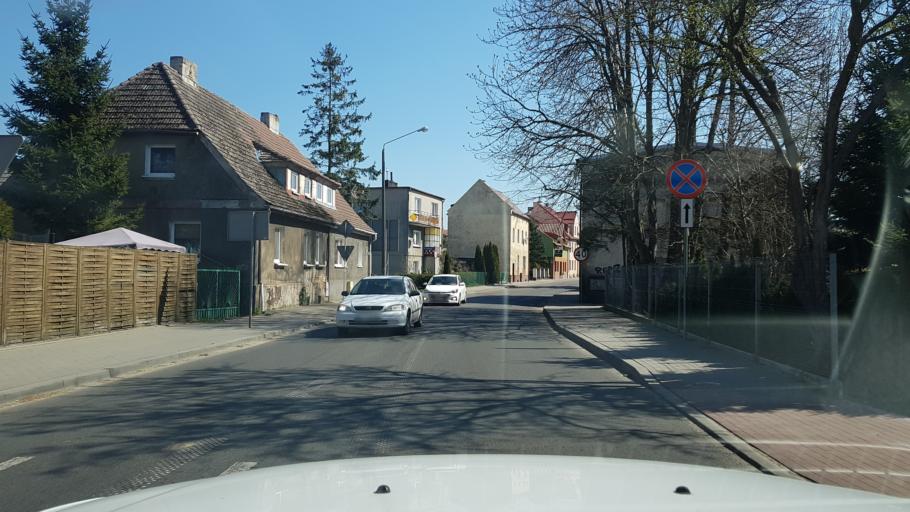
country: PL
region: West Pomeranian Voivodeship
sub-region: Powiat slawienski
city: Slawno
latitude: 54.3667
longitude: 16.6745
